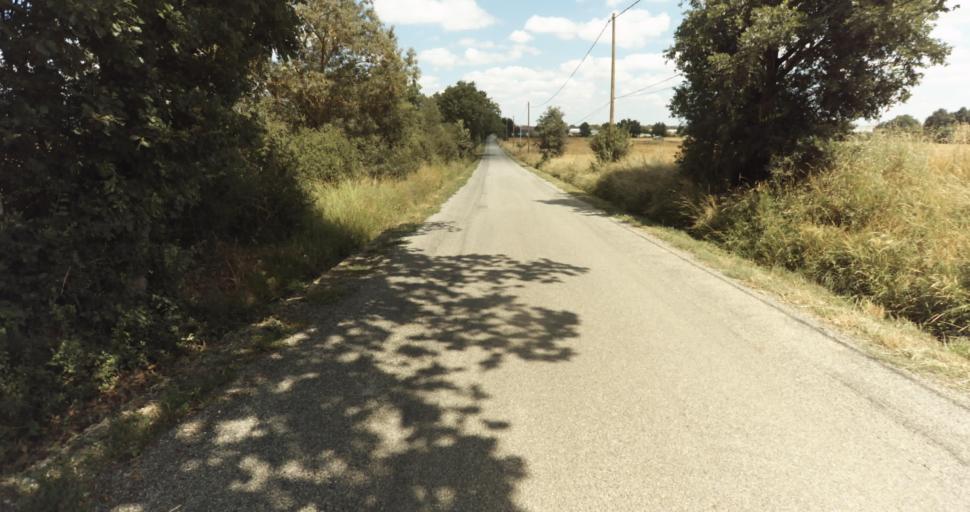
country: FR
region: Midi-Pyrenees
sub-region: Departement de la Haute-Garonne
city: Fontenilles
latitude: 43.5609
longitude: 1.1659
